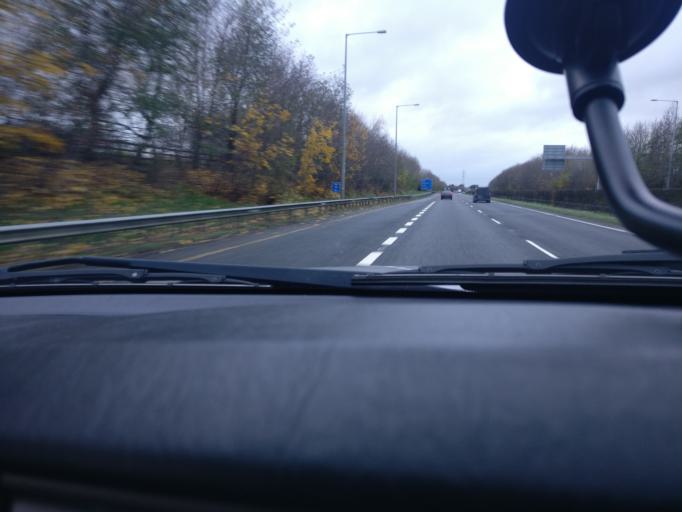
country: IE
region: Leinster
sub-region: Kildare
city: Celbridge
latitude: 53.3599
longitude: -6.5390
